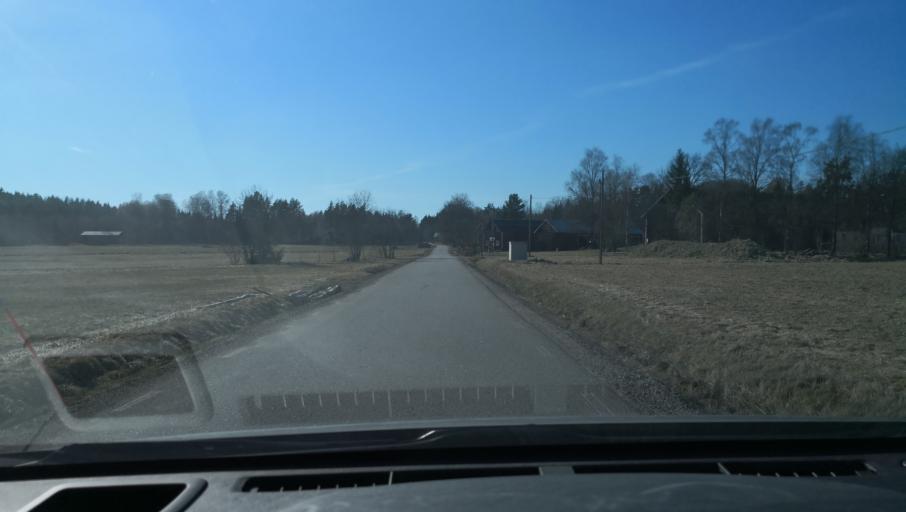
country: SE
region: Dalarna
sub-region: Avesta Kommun
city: Horndal
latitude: 60.0819
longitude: 16.4542
